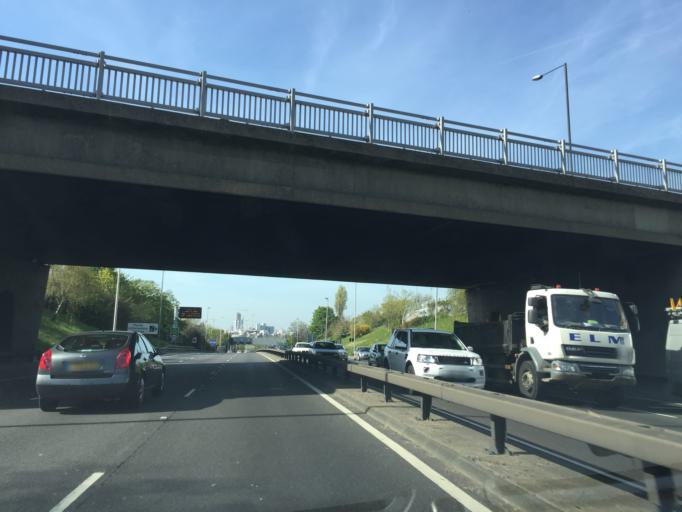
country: GB
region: England
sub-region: Greater London
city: Blackheath
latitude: 51.4783
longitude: 0.0226
